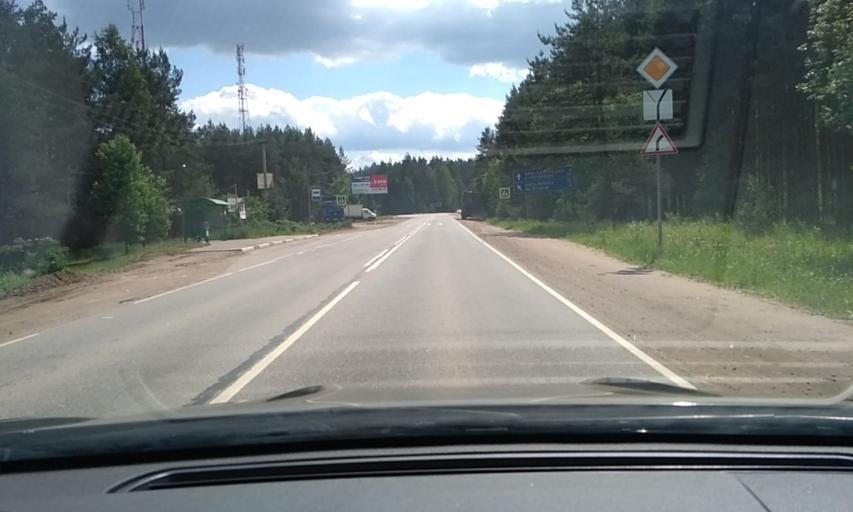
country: RU
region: Leningrad
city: Imeni Sverdlova
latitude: 59.8604
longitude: 30.6715
